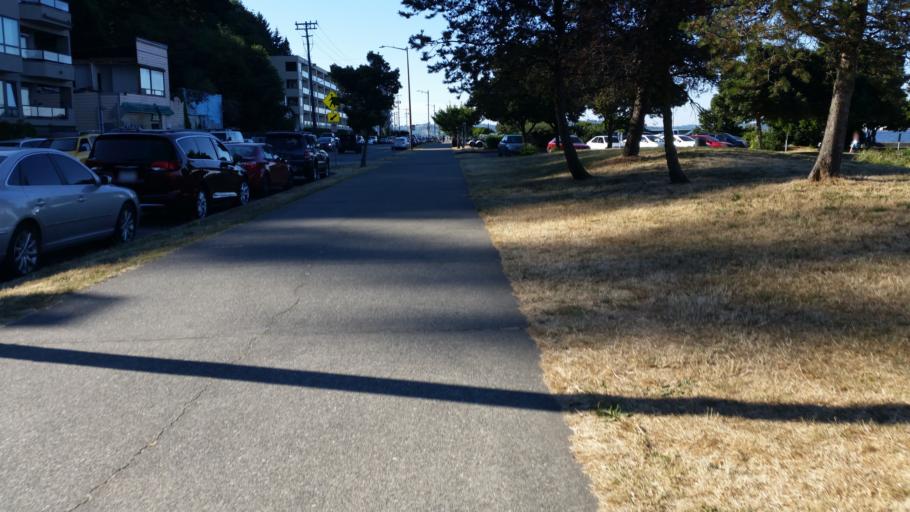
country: US
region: Washington
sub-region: King County
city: Seattle
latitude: 47.5909
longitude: -122.3821
